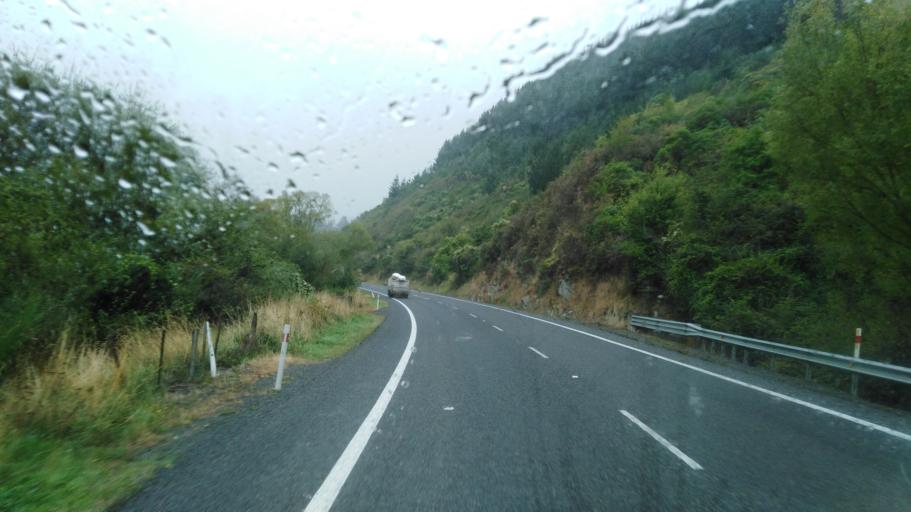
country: NZ
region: Marlborough
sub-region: Marlborough District
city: Picton
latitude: -41.3862
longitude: 173.9520
